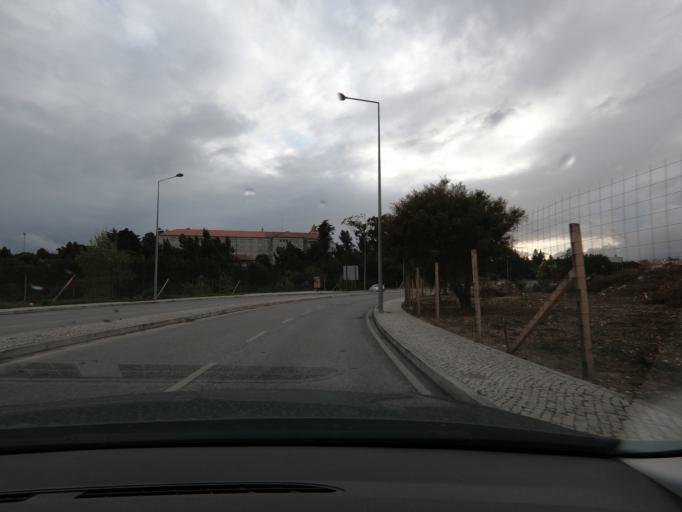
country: PT
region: Lisbon
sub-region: Cascais
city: Sao Domingos de Rana
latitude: 38.7102
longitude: -9.3318
